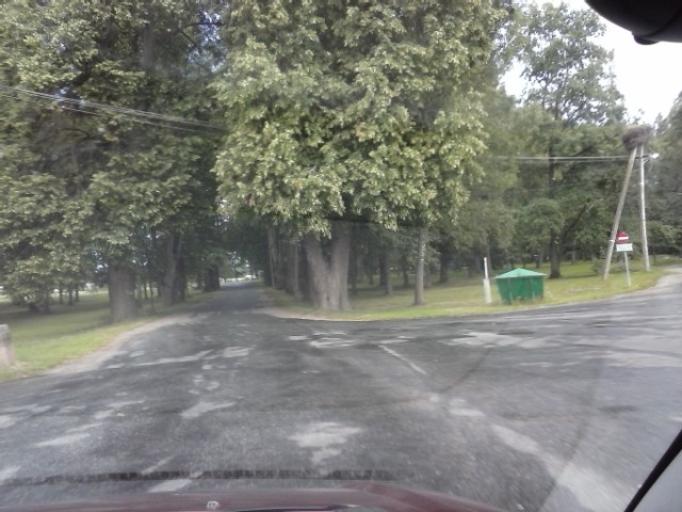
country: EE
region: Tartu
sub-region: Tartu linn
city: Tartu
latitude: 58.3563
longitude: 26.8822
